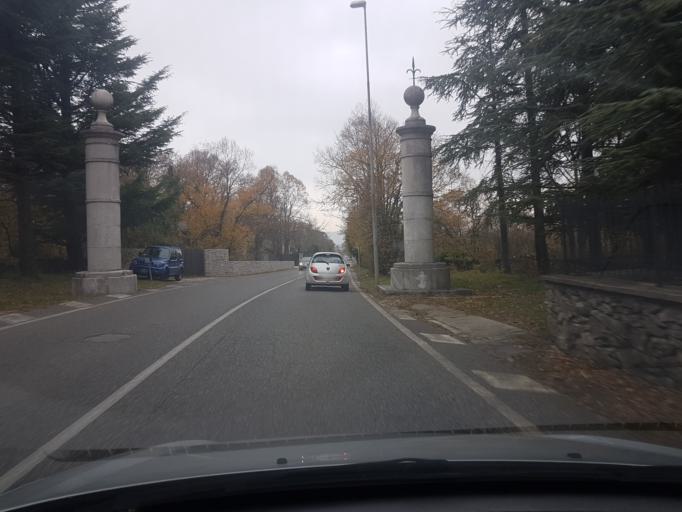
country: IT
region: Friuli Venezia Giulia
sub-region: Provincia di Trieste
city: Aurisina
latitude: 45.7445
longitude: 13.6791
